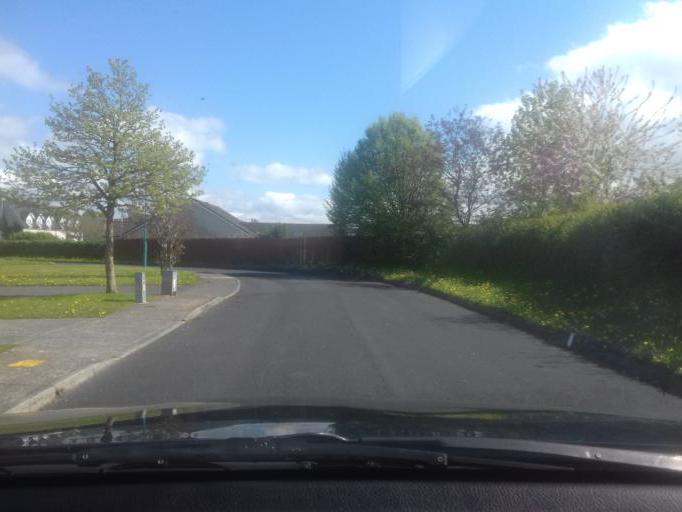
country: IE
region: Leinster
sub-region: Laois
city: Portlaoise
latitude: 53.0442
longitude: -7.2709
